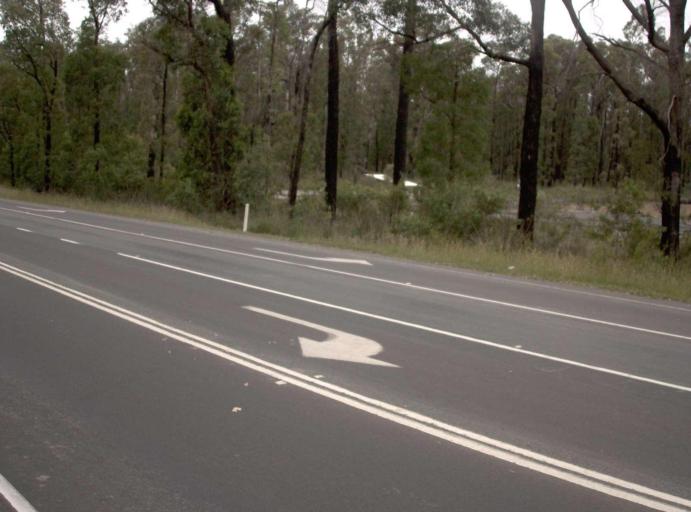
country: AU
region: Victoria
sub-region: Yarra Ranges
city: Yarra Glen
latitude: -37.5258
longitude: 145.4189
